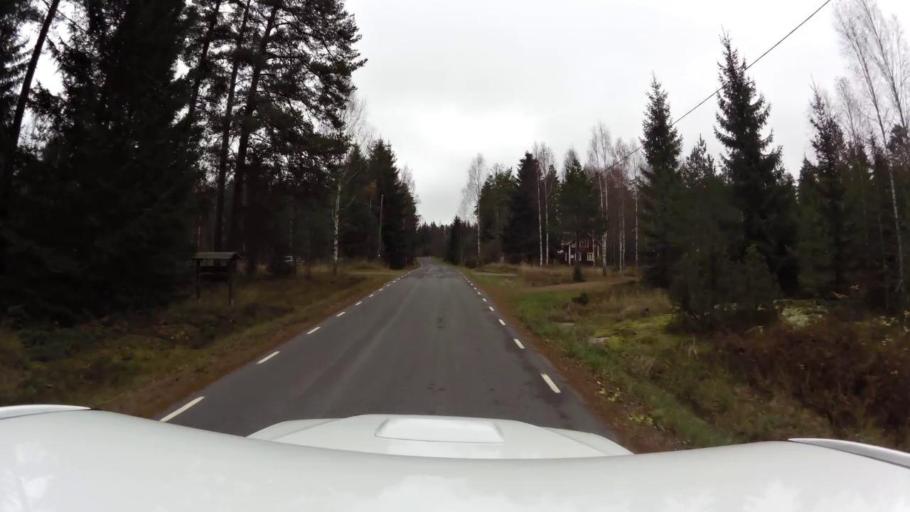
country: SE
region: OEstergoetland
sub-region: Kinda Kommun
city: Kisa
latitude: 58.1347
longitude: 15.4526
